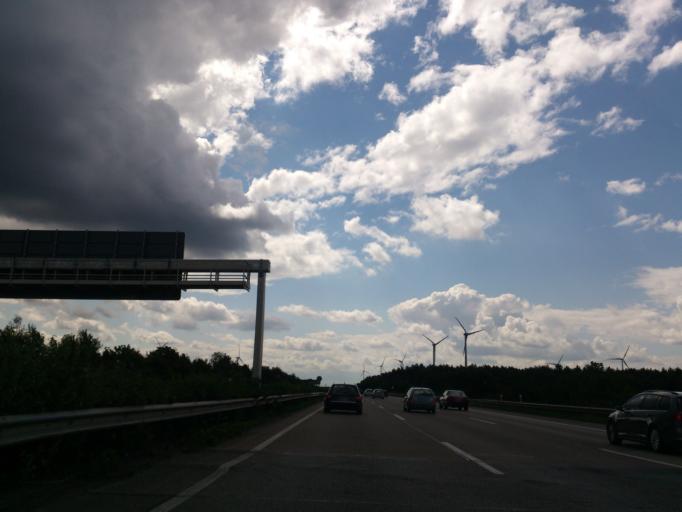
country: DE
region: Lower Saxony
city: Essel
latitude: 52.6695
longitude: 9.6952
